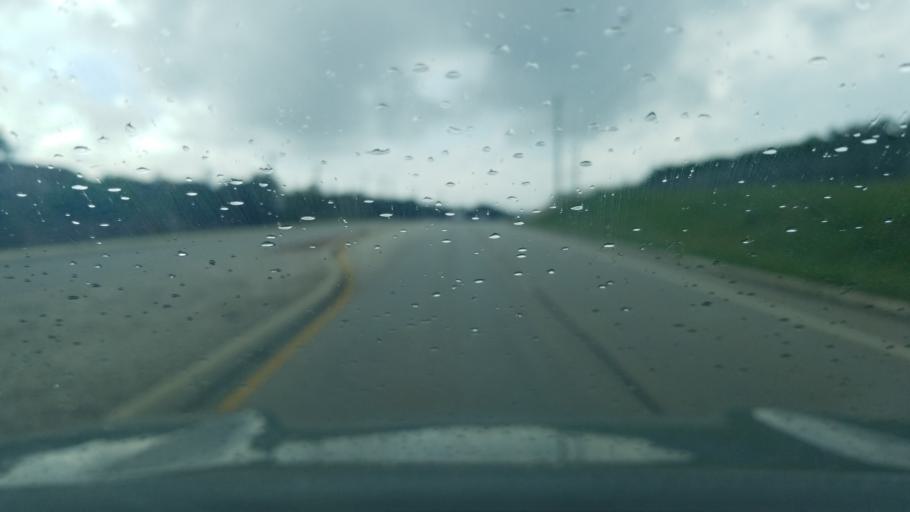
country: US
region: Texas
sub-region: Bexar County
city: Hollywood Park
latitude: 29.6472
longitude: -98.5184
